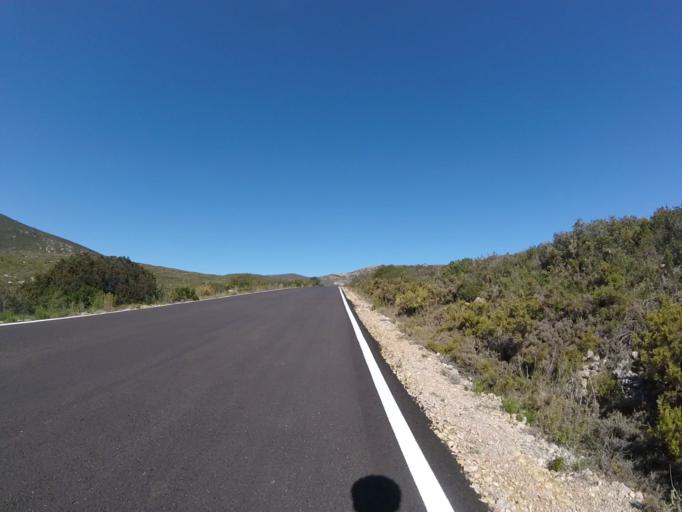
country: ES
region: Valencia
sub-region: Provincia de Castello
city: Cervera del Maestre
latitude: 40.4013
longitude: 0.2315
